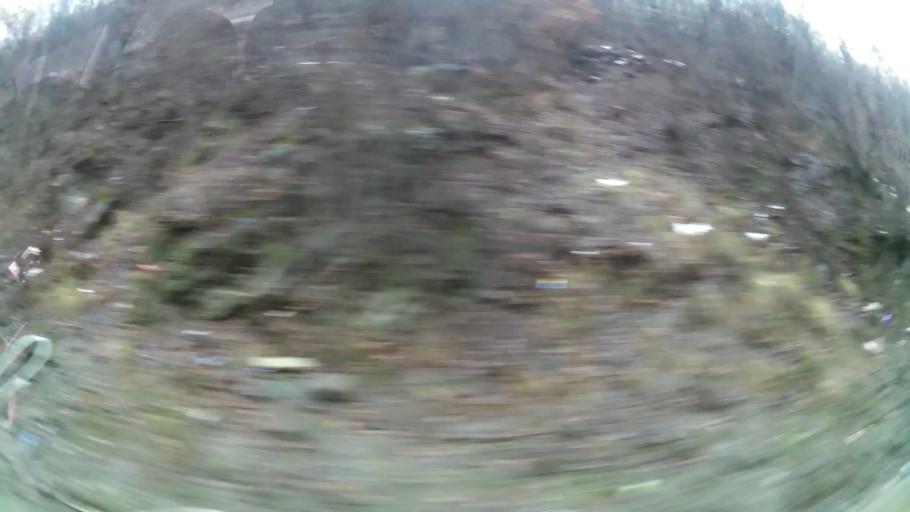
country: XK
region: Ferizaj
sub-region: Hani i Elezit
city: Hani i Elezit
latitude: 42.1675
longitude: 21.2776
